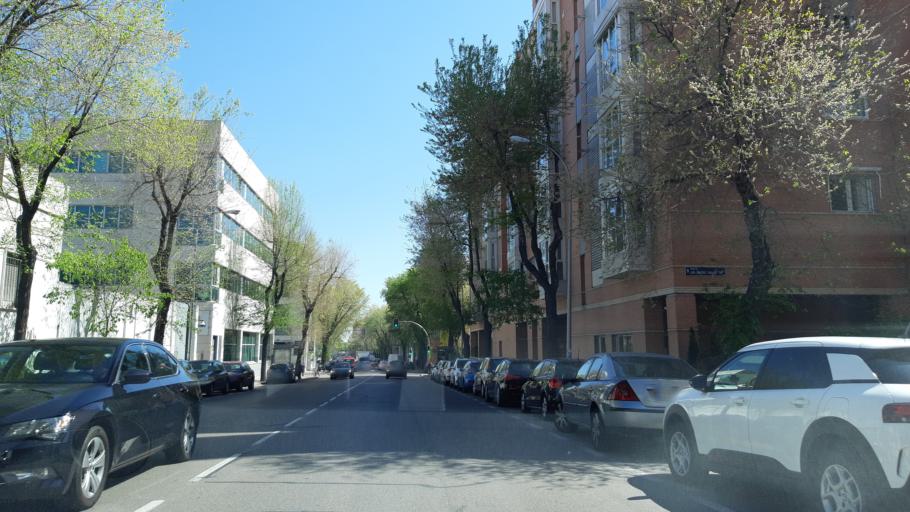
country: ES
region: Madrid
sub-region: Provincia de Madrid
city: San Blas
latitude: 40.4359
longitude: -3.6245
